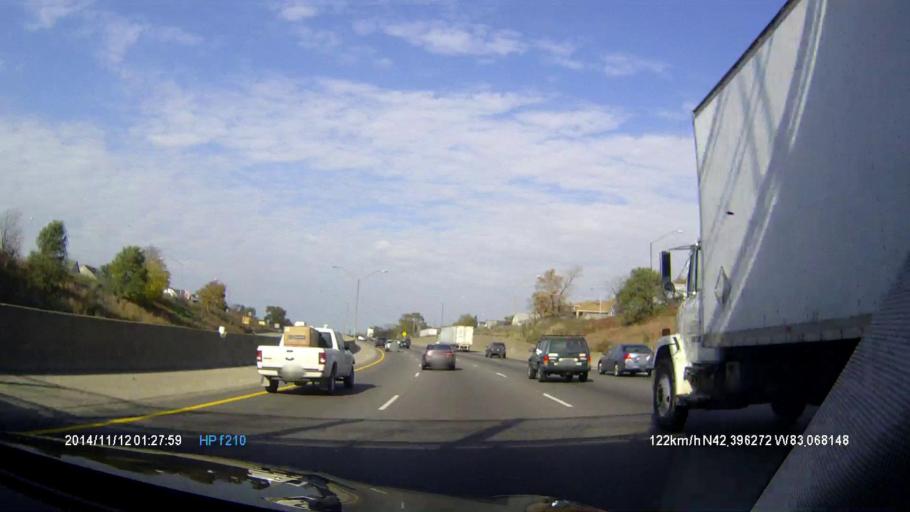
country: US
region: Michigan
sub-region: Wayne County
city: Hamtramck
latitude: 42.3966
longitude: -83.0682
